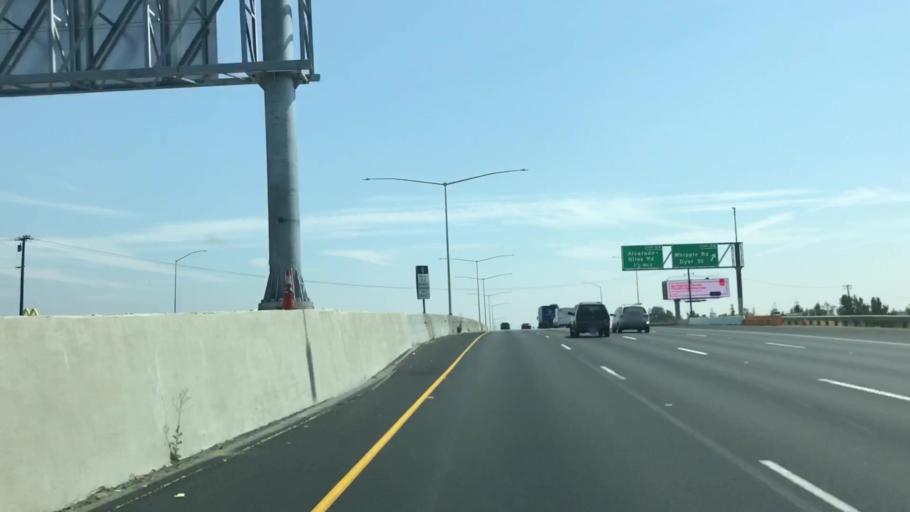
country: US
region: California
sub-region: Alameda County
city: Union City
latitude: 37.6091
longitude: -122.0687
